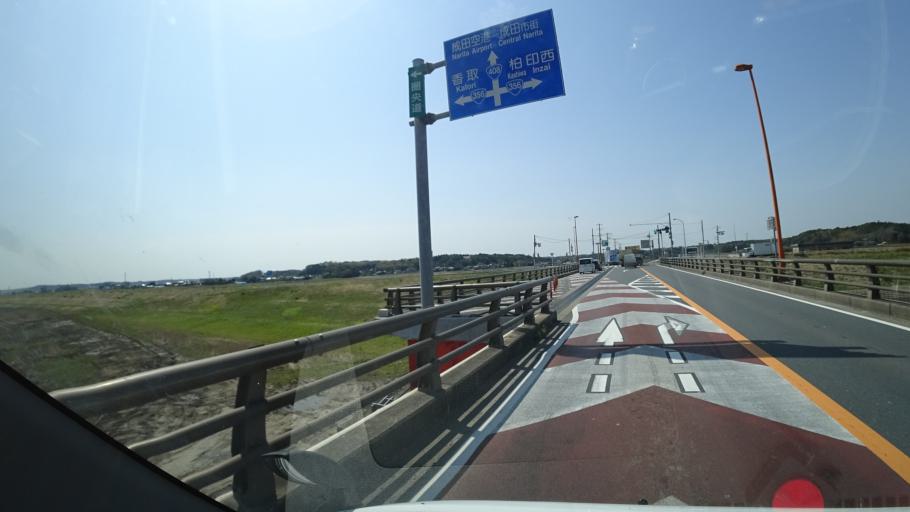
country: JP
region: Ibaraki
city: Edosaki
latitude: 35.8689
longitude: 140.2885
